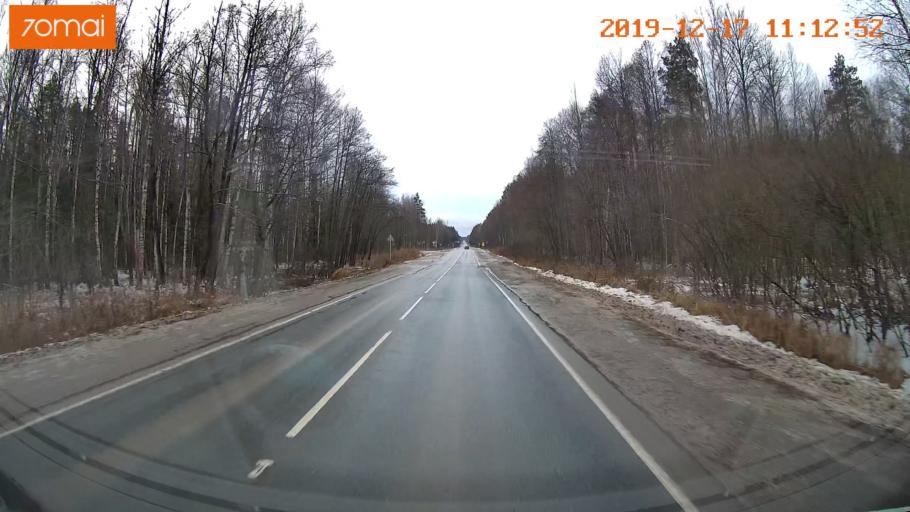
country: RU
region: Vladimir
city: Gus'-Khrustal'nyy
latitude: 55.5705
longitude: 40.6243
